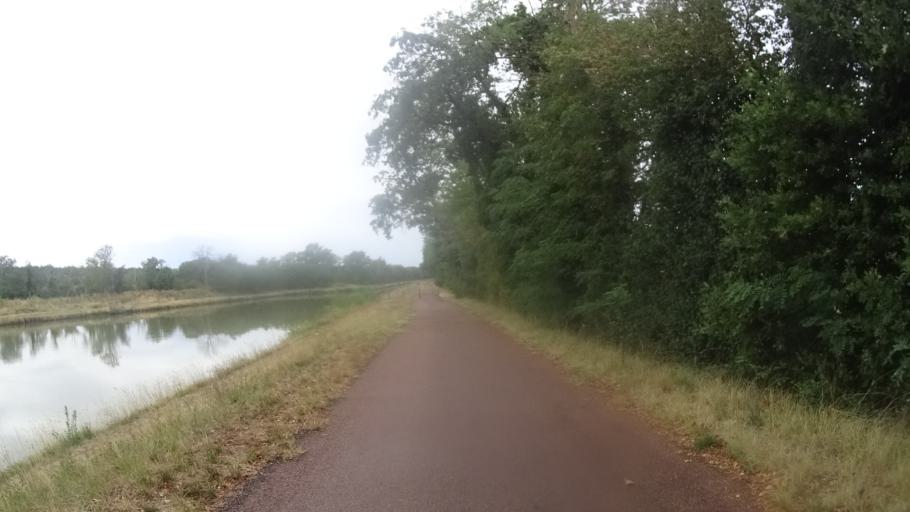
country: FR
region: Bourgogne
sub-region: Departement de la Nievre
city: Imphy
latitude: 46.8733
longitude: 3.2706
